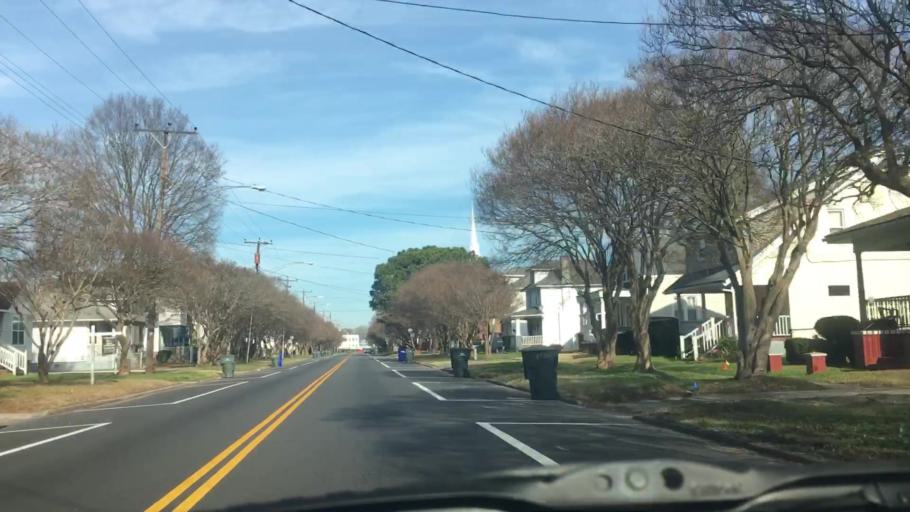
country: US
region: Virginia
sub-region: City of Norfolk
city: Norfolk
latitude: 36.8704
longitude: -76.2523
